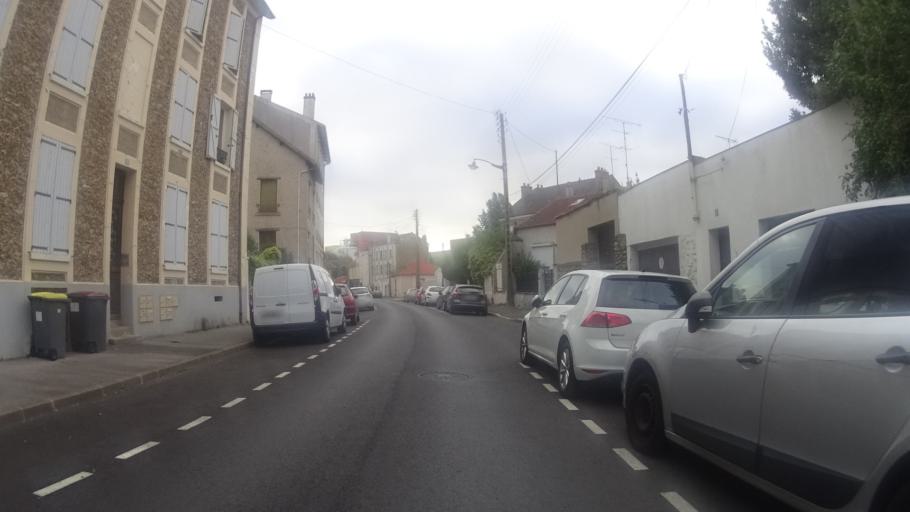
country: FR
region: Ile-de-France
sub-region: Departement de l'Essonne
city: Corbeil-Essonnes
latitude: 48.6107
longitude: 2.4727
